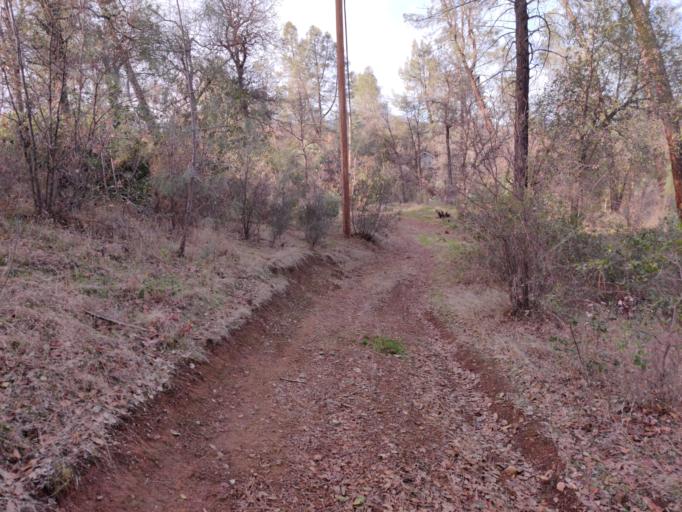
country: US
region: California
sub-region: Shasta County
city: Shasta Lake
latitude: 40.6690
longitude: -122.3542
